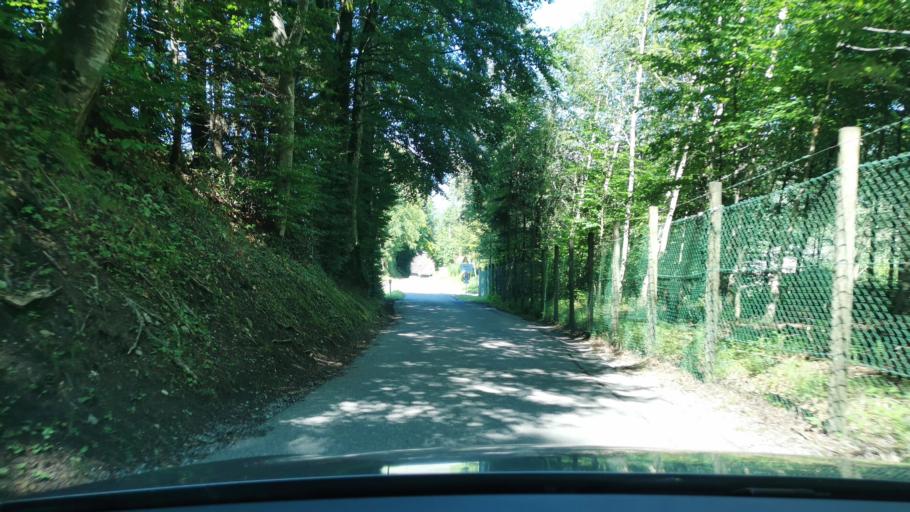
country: AT
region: Vorarlberg
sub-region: Politischer Bezirk Feldkirch
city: Viktorsberg
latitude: 47.2873
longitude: 9.6708
